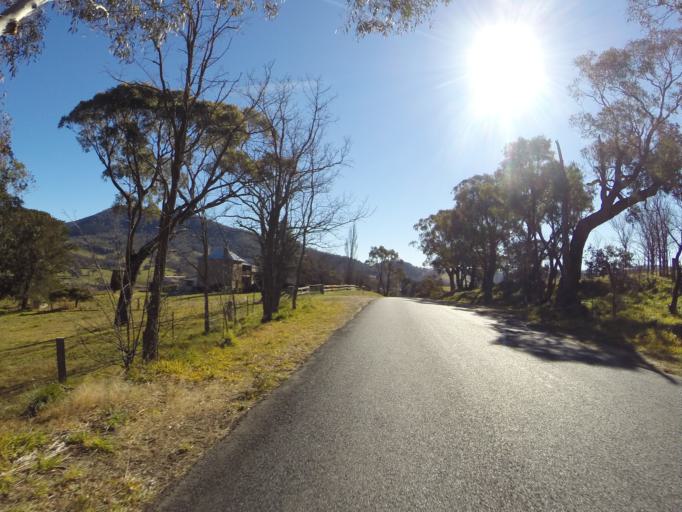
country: AU
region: New South Wales
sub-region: Oberon
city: Oberon
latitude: -33.5328
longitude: 149.9032
